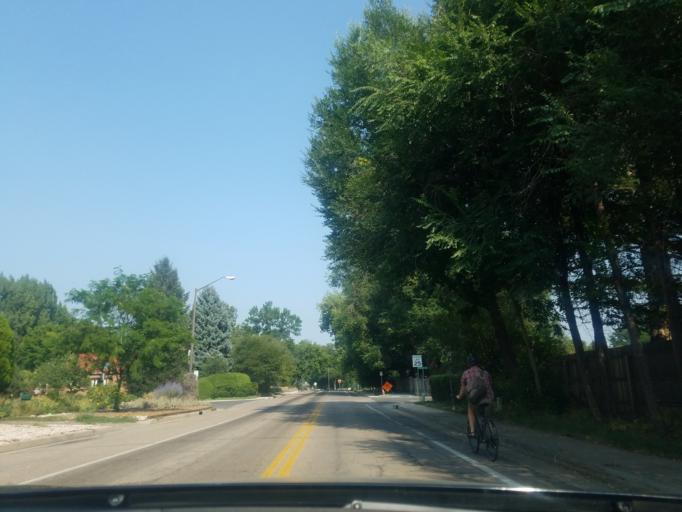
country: US
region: Colorado
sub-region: Larimer County
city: Fort Collins
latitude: 40.5710
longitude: -105.0690
